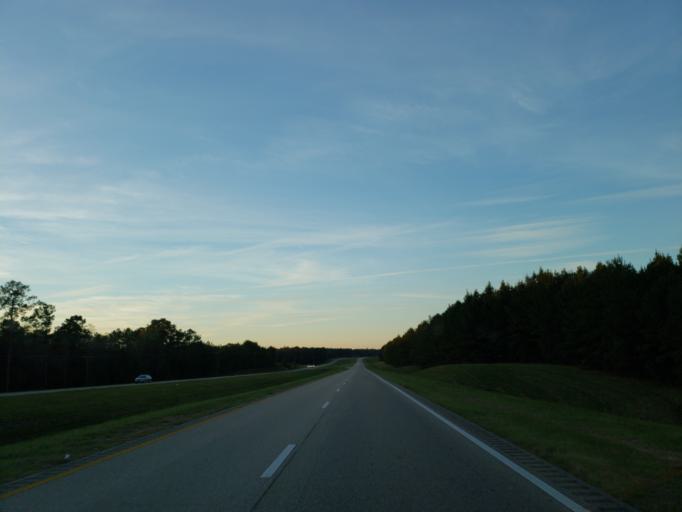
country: US
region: Mississippi
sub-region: Wayne County
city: Belmont
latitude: 31.4805
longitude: -88.4825
